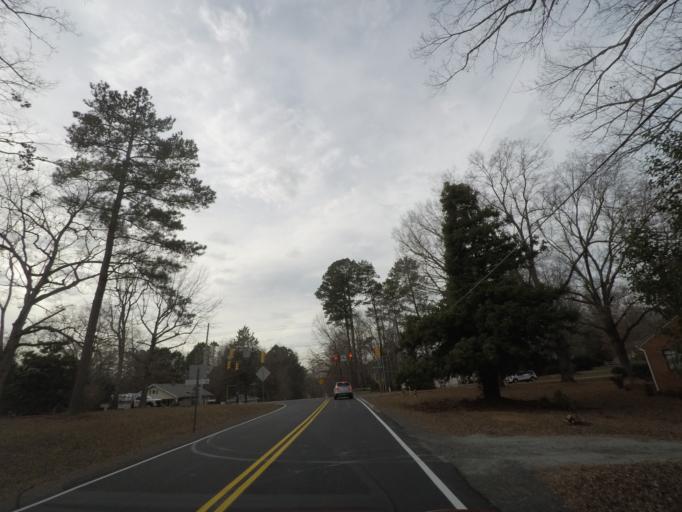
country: US
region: North Carolina
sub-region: Durham County
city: Durham
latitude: 36.0428
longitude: -78.9566
